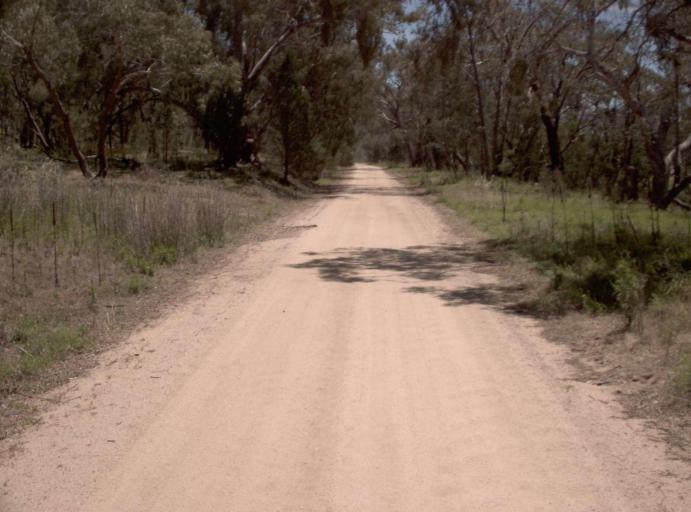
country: AU
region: New South Wales
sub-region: Snowy River
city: Jindabyne
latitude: -36.8858
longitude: 148.4189
